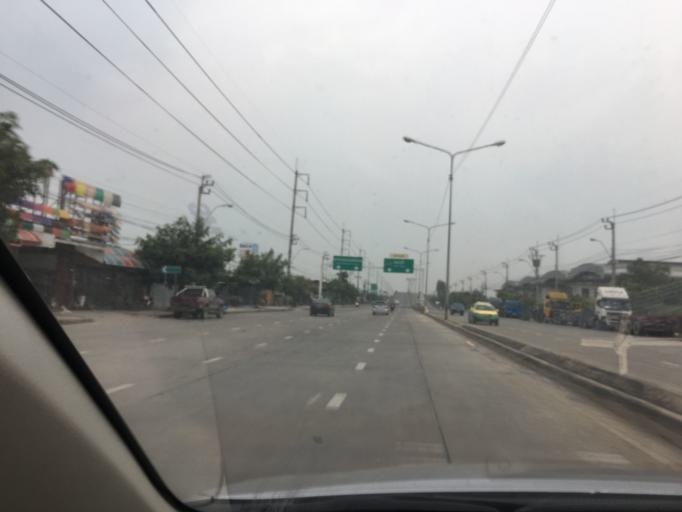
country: TH
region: Bangkok
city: Lat Krabang
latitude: 13.7538
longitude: 100.7656
